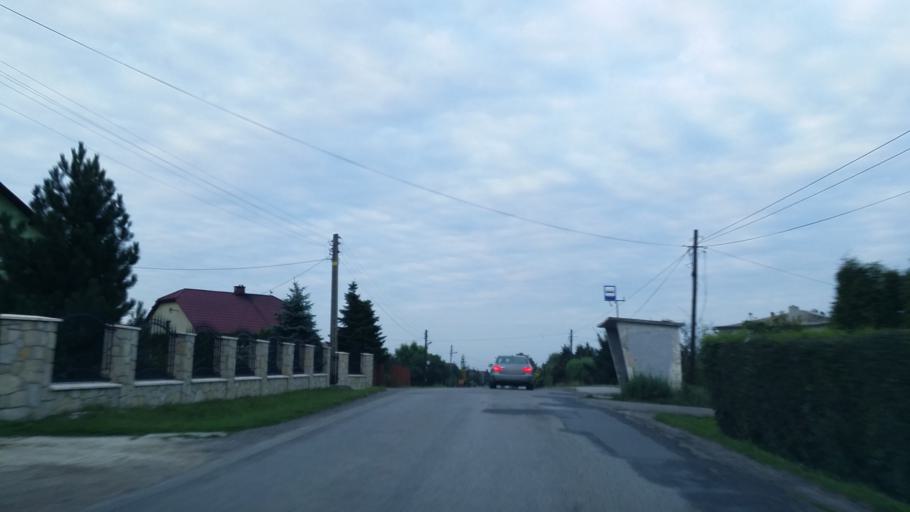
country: PL
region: Lesser Poland Voivodeship
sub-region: Powiat krakowski
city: Kaszow
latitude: 50.0153
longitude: 19.7181
